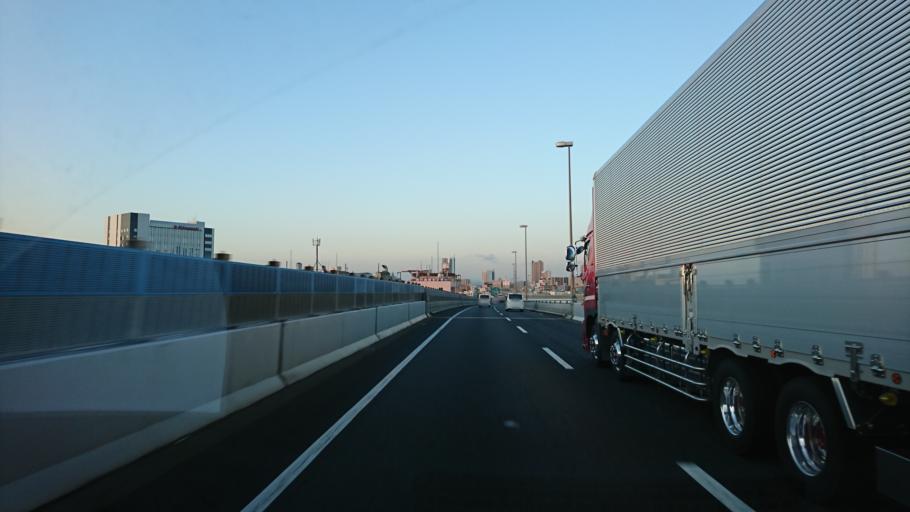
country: JP
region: Hyogo
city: Kobe
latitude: 34.6627
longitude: 135.1608
